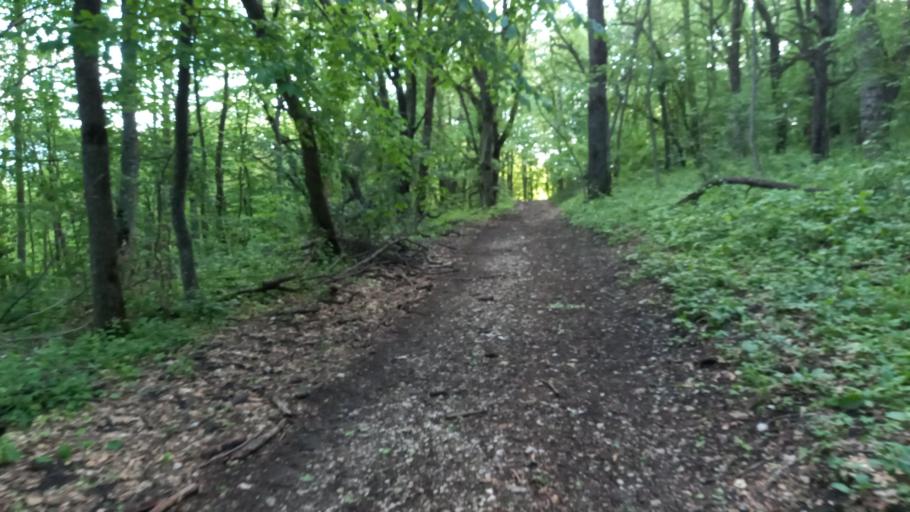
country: RU
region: Adygeya
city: Kamennomostskiy
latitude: 44.2195
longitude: 40.0056
